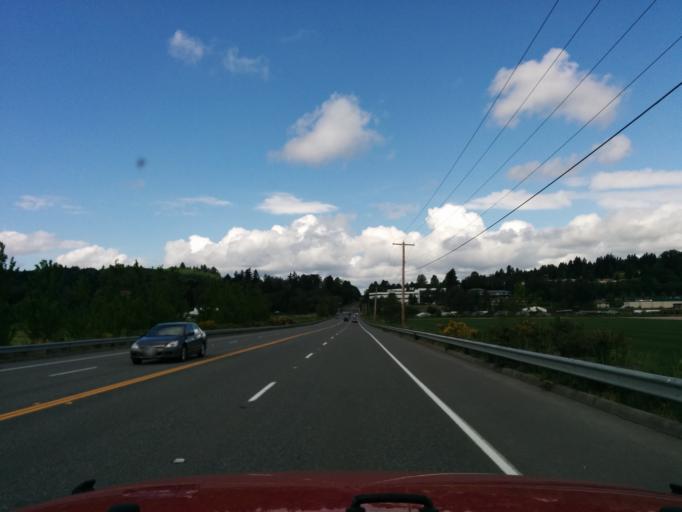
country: US
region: Washington
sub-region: King County
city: Kingsgate
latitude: 47.7113
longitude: -122.1454
